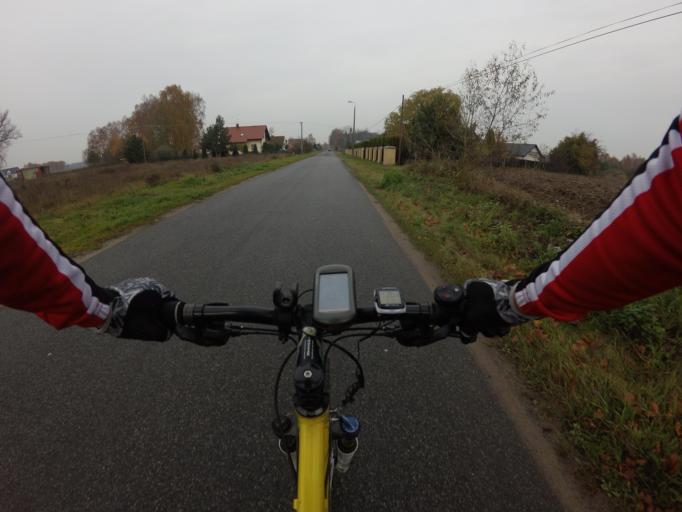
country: PL
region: Kujawsko-Pomorskie
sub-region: Powiat bydgoski
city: Osielsko
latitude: 53.2226
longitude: 18.0584
